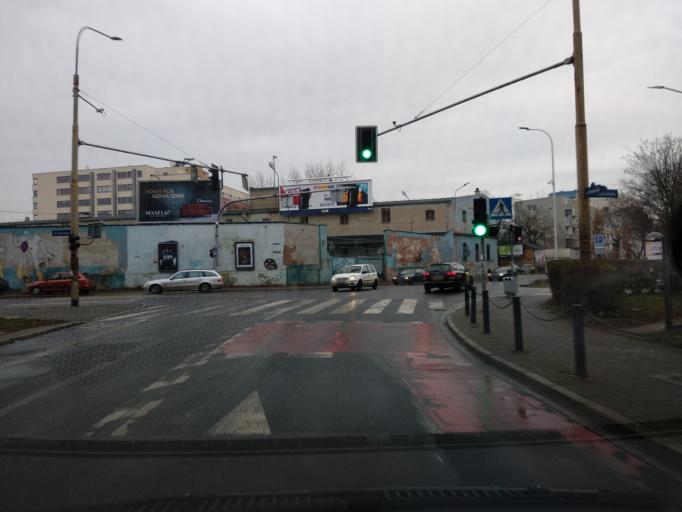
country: PL
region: Lower Silesian Voivodeship
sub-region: Powiat wroclawski
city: Wroclaw
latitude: 51.1105
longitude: 17.0171
